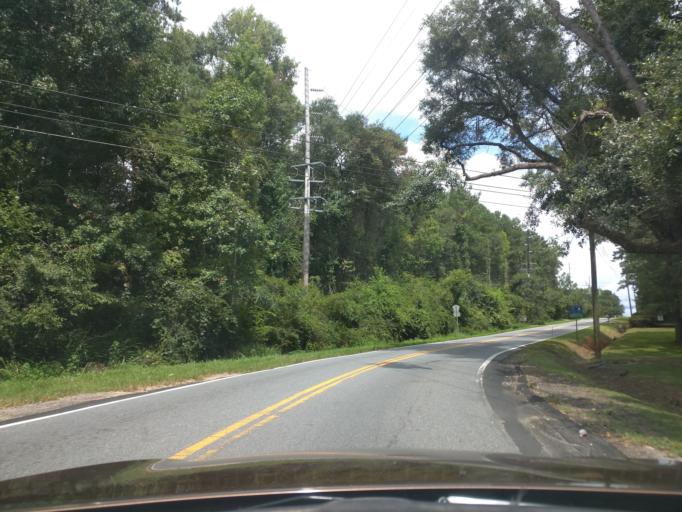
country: US
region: Florida
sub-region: Leon County
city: Tallahassee
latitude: 30.5382
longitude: -84.1763
